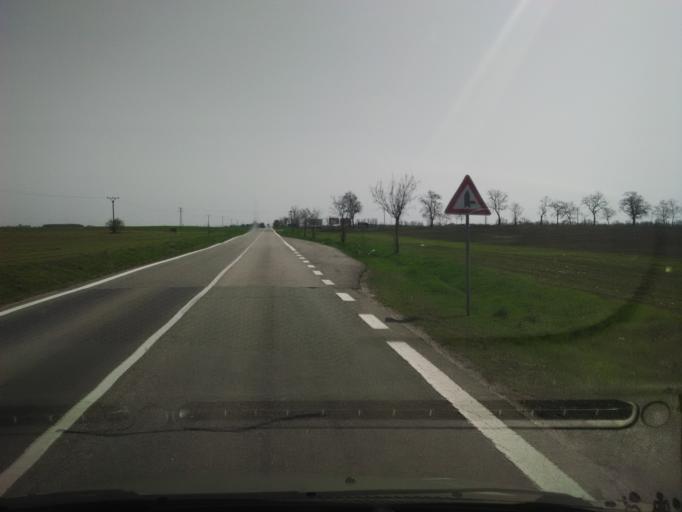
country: SK
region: Nitriansky
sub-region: Okres Nove Zamky
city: Nove Zamky
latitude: 48.0414
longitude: 18.1214
